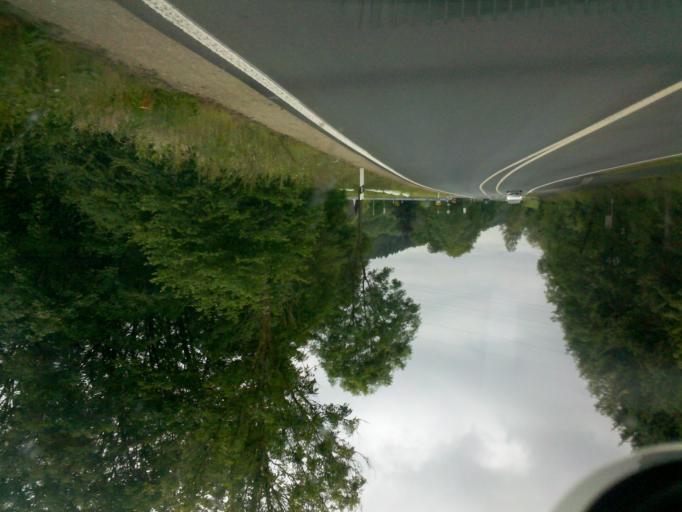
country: DE
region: North Rhine-Westphalia
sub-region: Regierungsbezirk Arnsberg
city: Lennestadt
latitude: 51.1693
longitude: 8.1108
